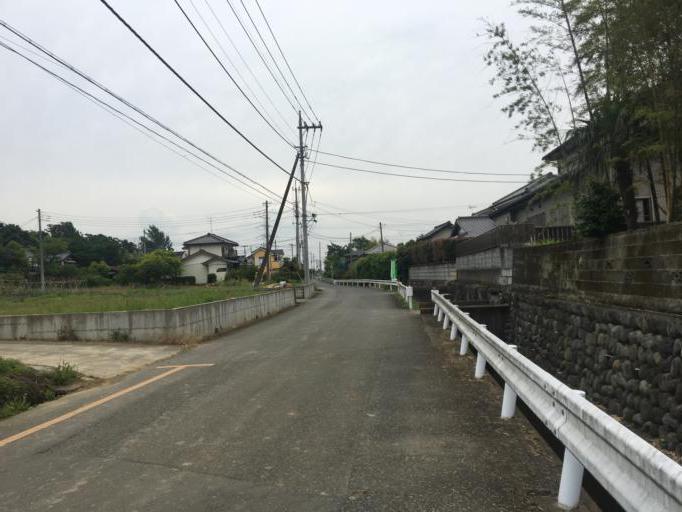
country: JP
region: Saitama
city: Fukiage-fujimi
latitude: 36.0223
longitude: 139.4516
